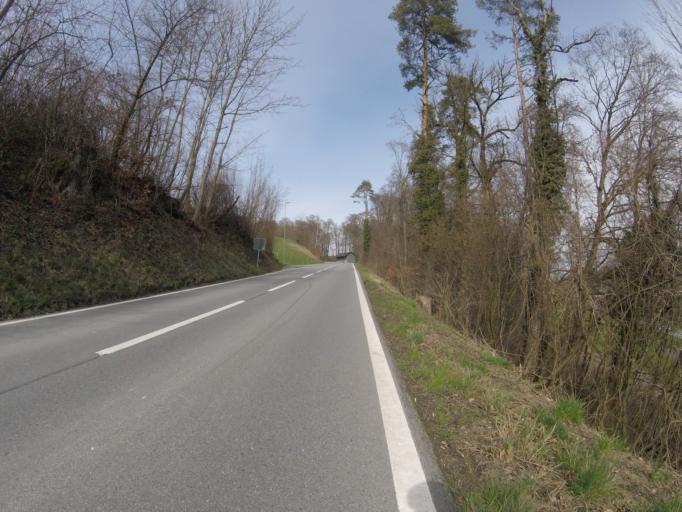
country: CH
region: Bern
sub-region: Bern-Mittelland District
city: Laupen
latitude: 46.9144
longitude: 7.2337
